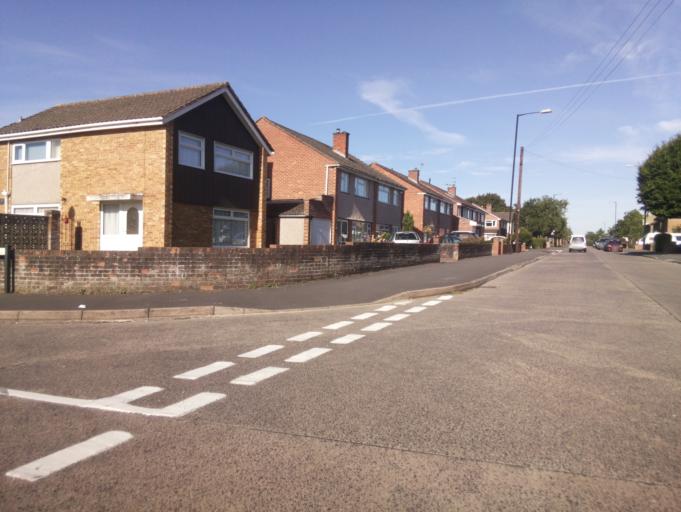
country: GB
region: England
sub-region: Bath and North East Somerset
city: Whitchurch
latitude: 51.4117
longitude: -2.5433
